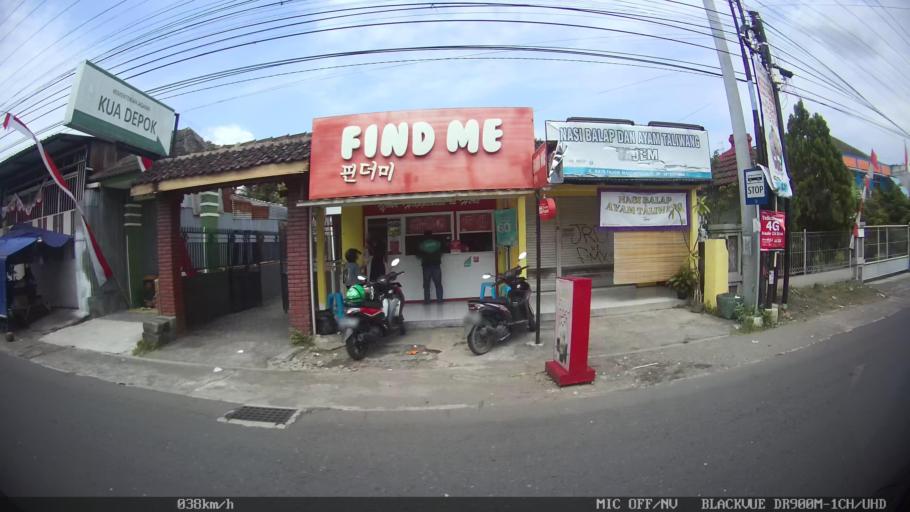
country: ID
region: Daerah Istimewa Yogyakarta
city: Depok
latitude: -7.7551
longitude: 110.4339
